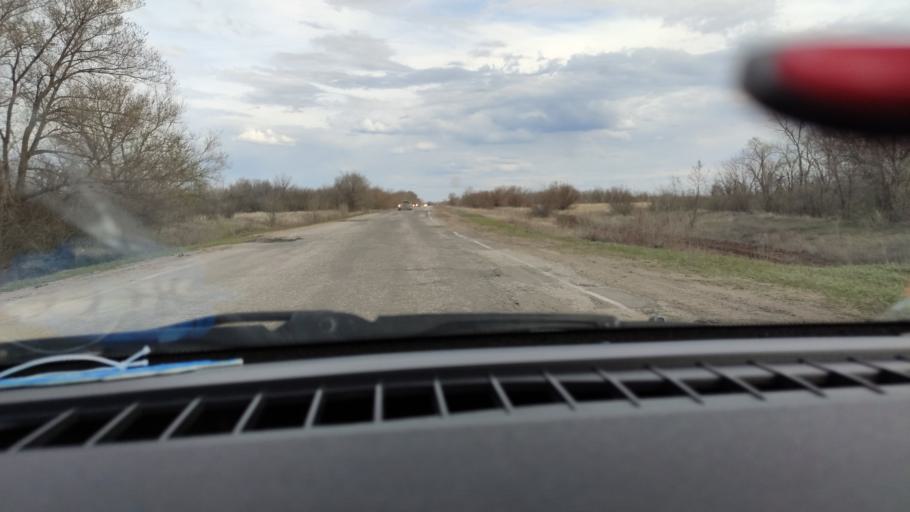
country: RU
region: Saratov
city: Rovnoye
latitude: 51.0421
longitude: 46.0651
